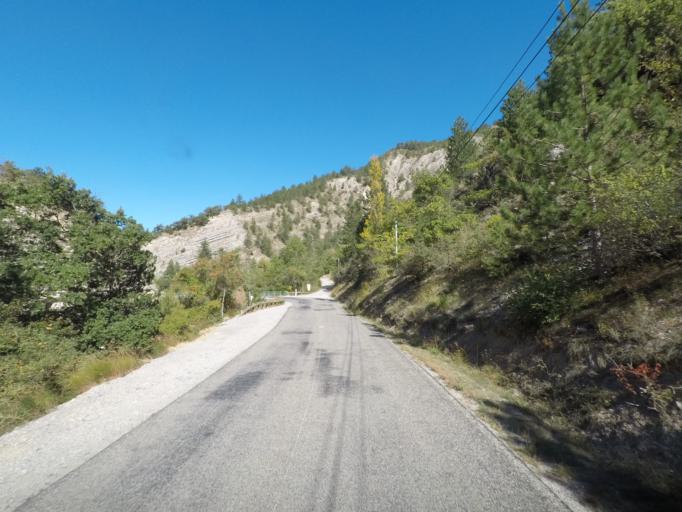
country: FR
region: Rhone-Alpes
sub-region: Departement de la Drome
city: Die
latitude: 44.6525
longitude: 5.2870
